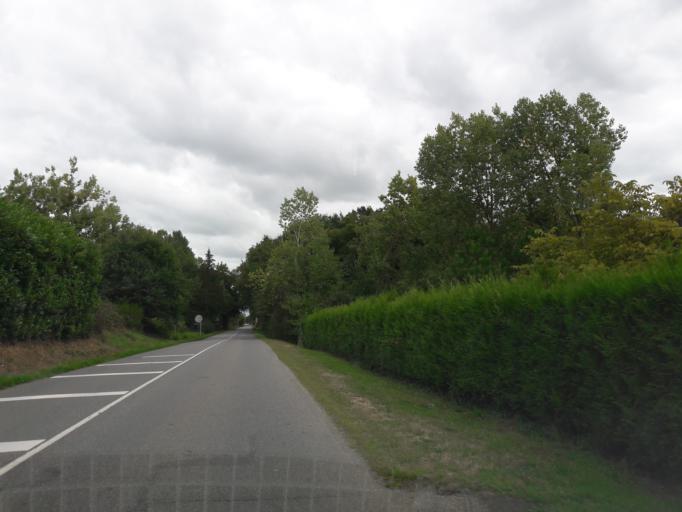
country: FR
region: Brittany
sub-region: Departement d'Ille-et-Vilaine
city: Chartres-de-Bretagne
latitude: 48.0217
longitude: -1.7147
